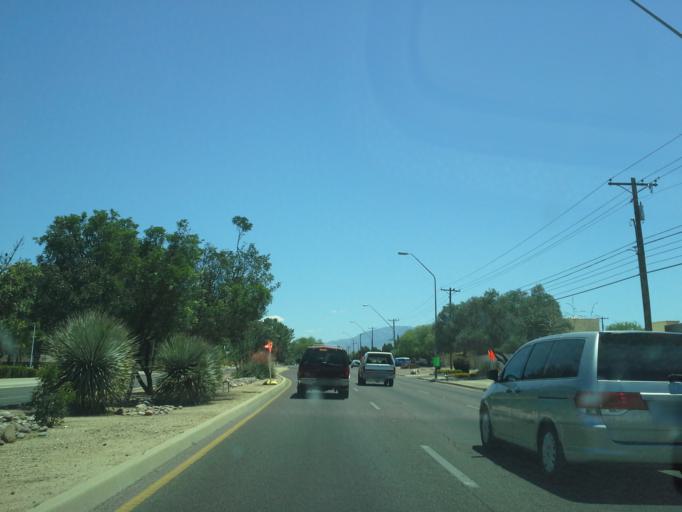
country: US
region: Arizona
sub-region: Pima County
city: Tucson
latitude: 32.2507
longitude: -110.8720
